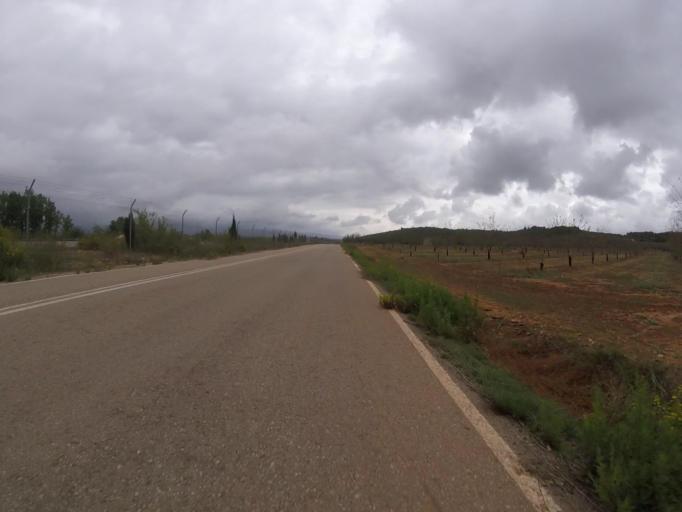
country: ES
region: Valencia
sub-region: Provincia de Castello
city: Cabanes
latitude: 40.1787
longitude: 0.0451
